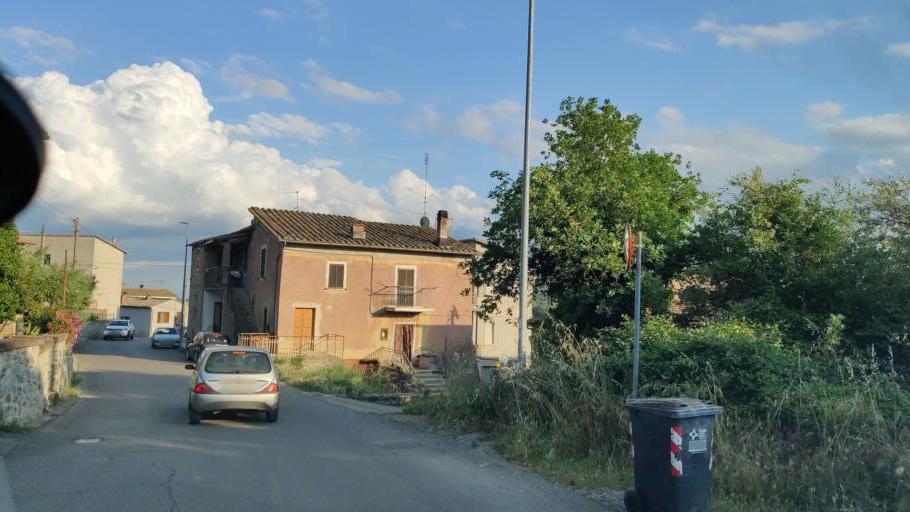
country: IT
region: Umbria
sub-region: Provincia di Terni
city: Lugnano in Teverina
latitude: 42.5962
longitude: 12.3675
